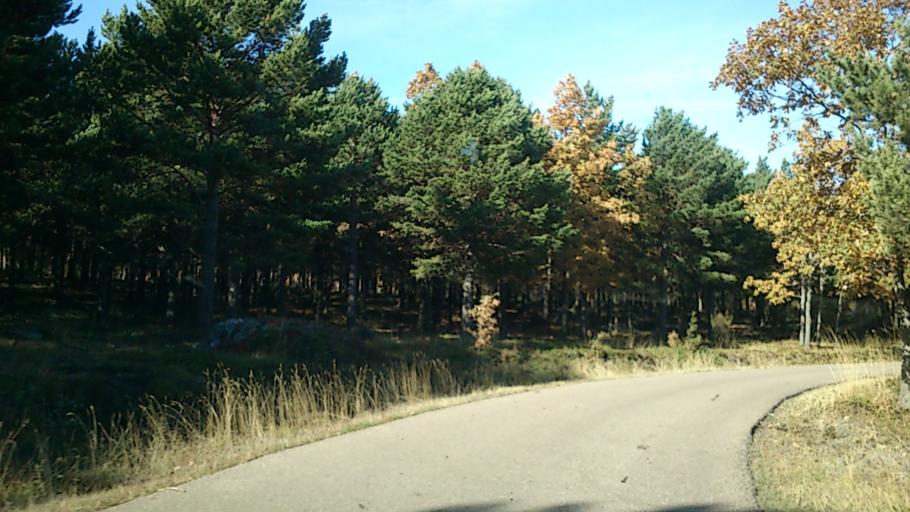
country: ES
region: Aragon
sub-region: Provincia de Zaragoza
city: Litago
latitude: 41.8032
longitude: -1.7882
